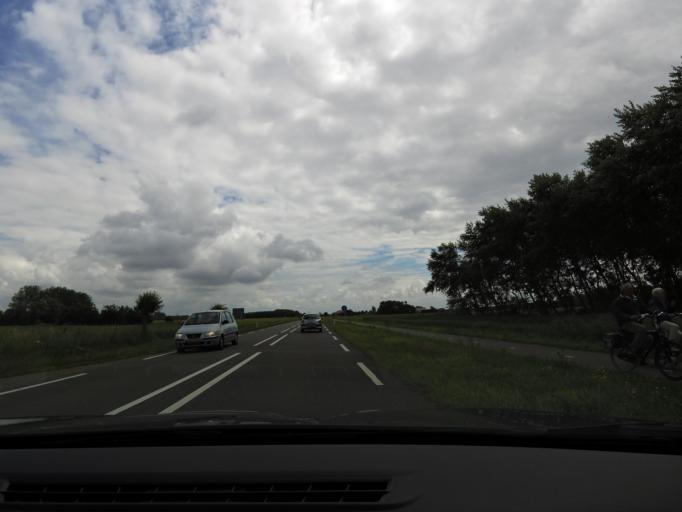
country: NL
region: Zeeland
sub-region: Gemeente Vlissingen
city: Vlissingen
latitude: 51.4936
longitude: 3.5226
